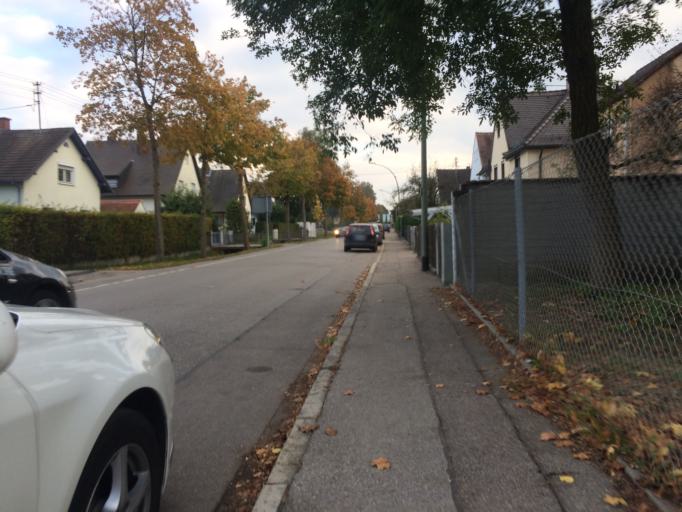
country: DE
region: Bavaria
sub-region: Swabia
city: Friedberg
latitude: 48.3558
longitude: 10.9733
